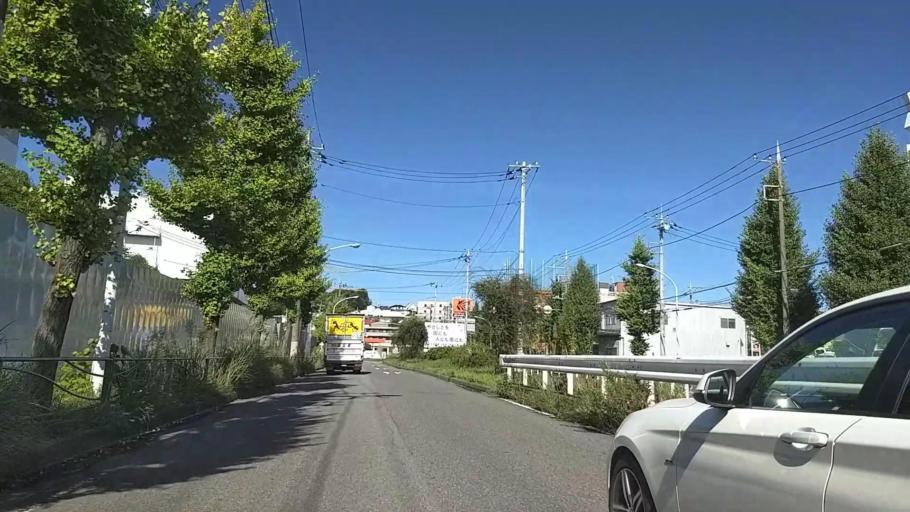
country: JP
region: Tokyo
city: Chofugaoka
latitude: 35.5821
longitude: 139.6066
